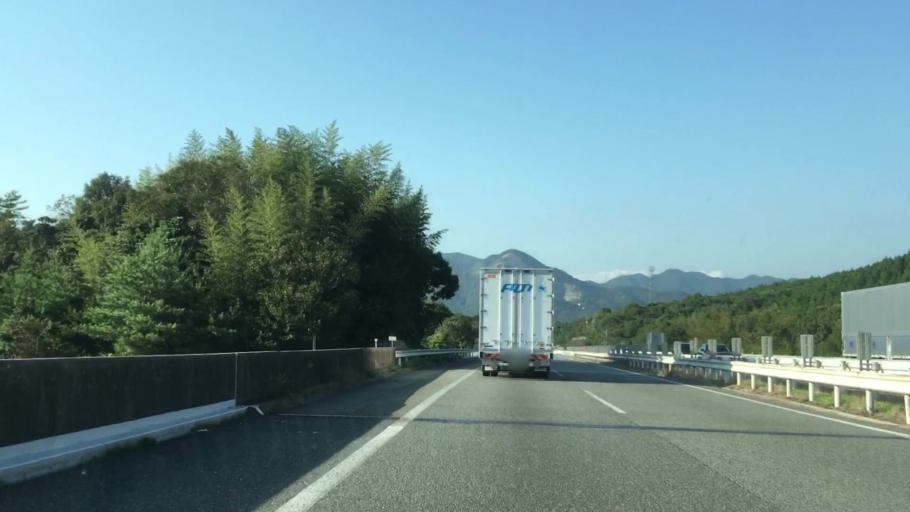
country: JP
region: Yamaguchi
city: Hofu
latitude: 34.0600
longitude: 131.5029
